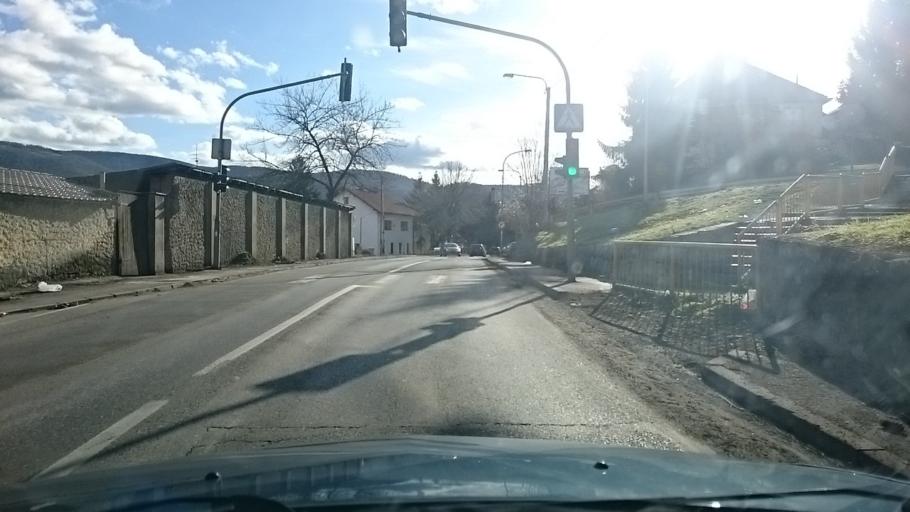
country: BA
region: Republika Srpska
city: Banja Luka
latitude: 44.7699
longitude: 17.1816
